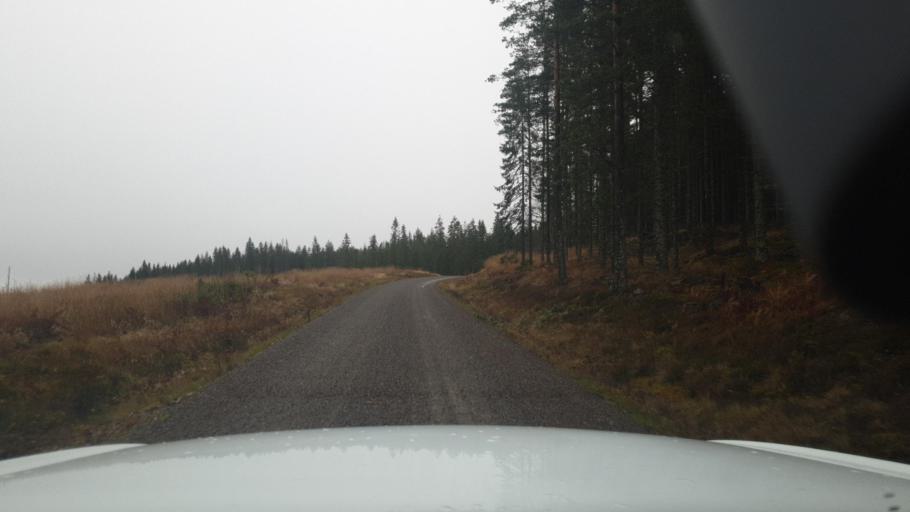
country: SE
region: Vaermland
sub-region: Eda Kommun
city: Charlottenberg
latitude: 60.0462
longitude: 12.6300
